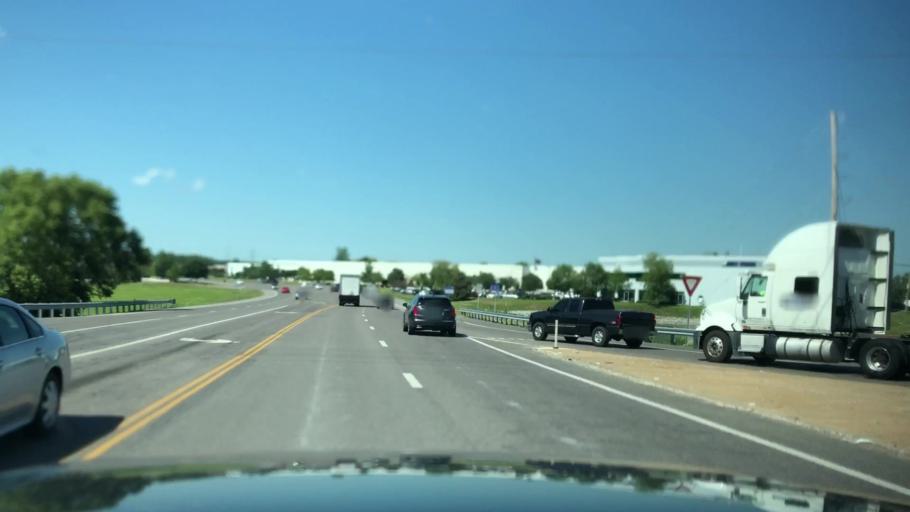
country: US
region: Missouri
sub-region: Saint Charles County
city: Saint Charles
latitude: 38.7793
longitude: -90.4594
